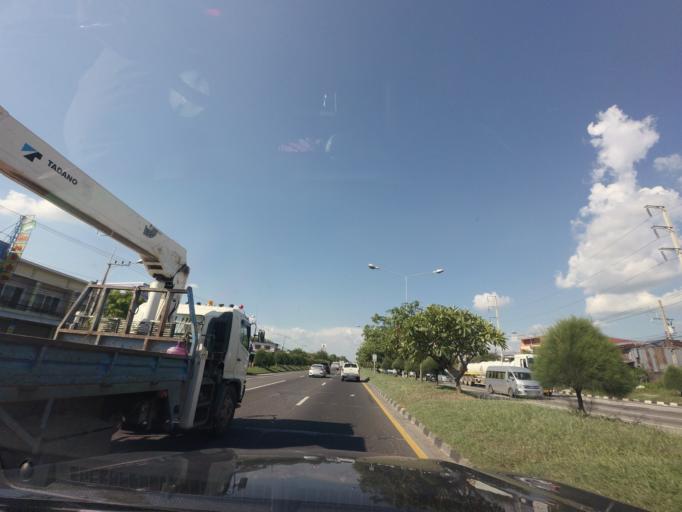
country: TH
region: Nakhon Ratchasima
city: Sida
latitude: 15.5476
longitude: 102.5480
